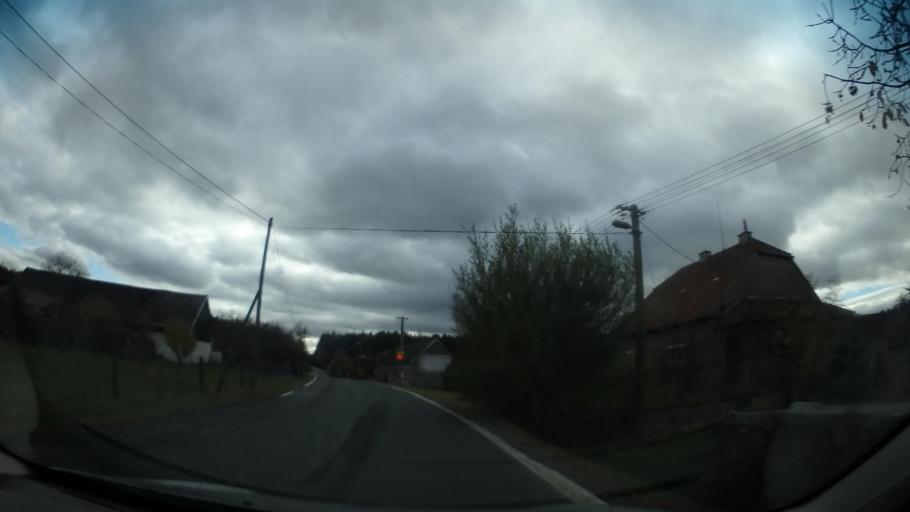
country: CZ
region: Vysocina
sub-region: Okres Zd'ar nad Sazavou
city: Velka Bites
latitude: 49.2555
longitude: 16.2575
